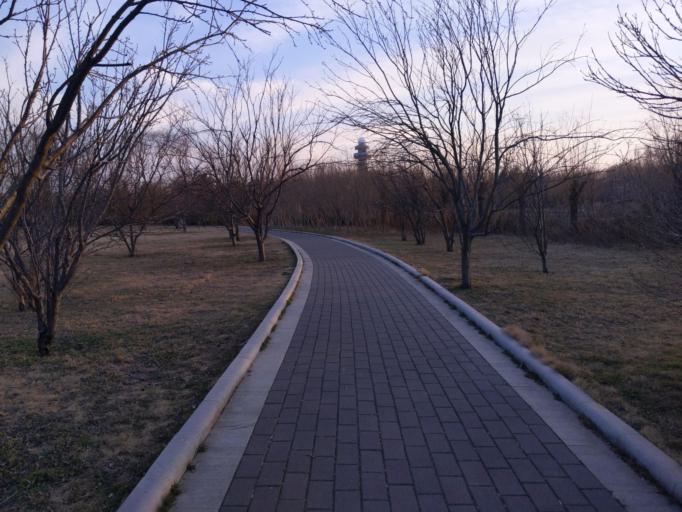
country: CN
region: Henan Sheng
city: Puyang
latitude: 35.7823
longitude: 114.9468
